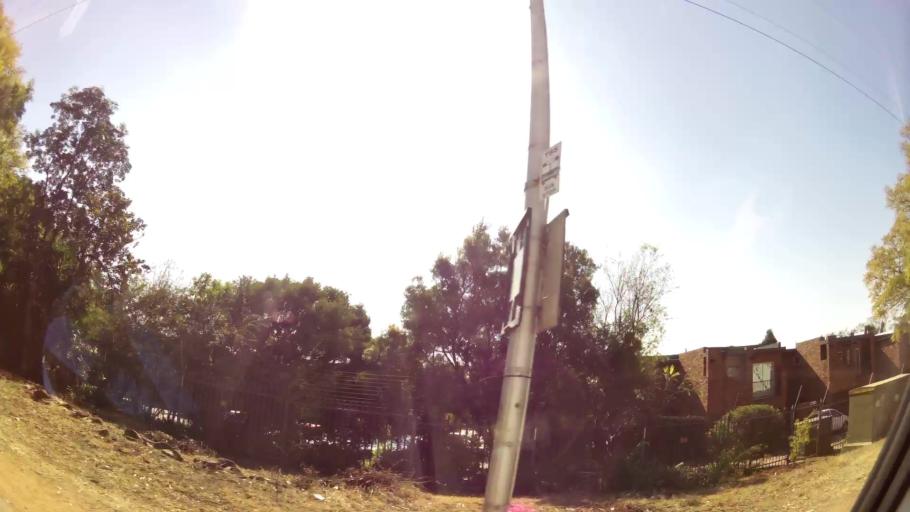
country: ZA
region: Gauteng
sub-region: City of Tshwane Metropolitan Municipality
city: Pretoria
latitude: -25.7828
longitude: 28.2606
